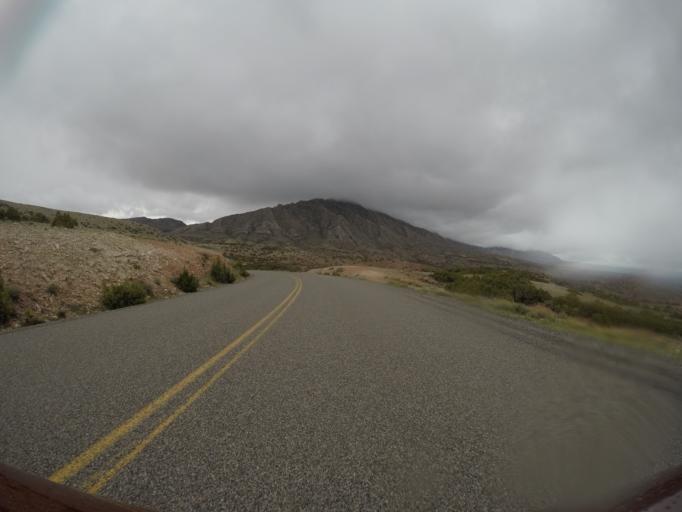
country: US
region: Wyoming
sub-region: Big Horn County
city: Lovell
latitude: 45.0244
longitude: -108.2557
